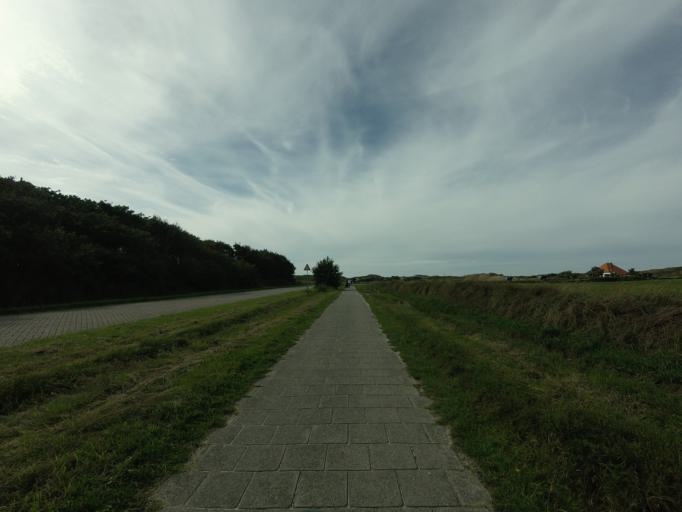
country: NL
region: North Holland
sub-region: Gemeente Texel
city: Den Burg
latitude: 53.0771
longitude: 4.7506
